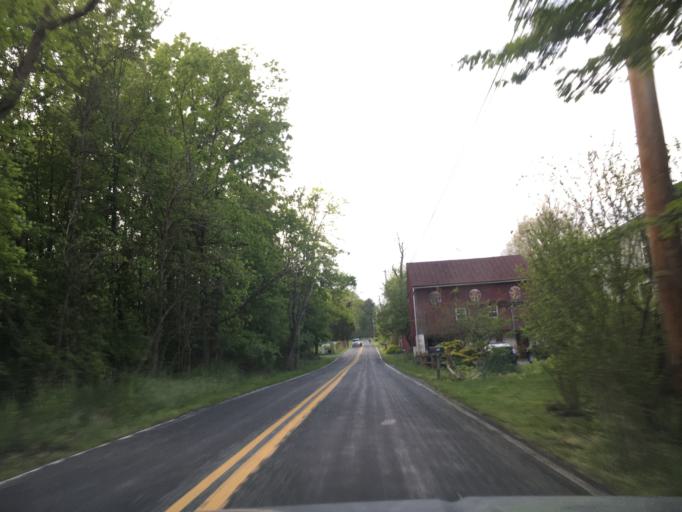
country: US
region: Pennsylvania
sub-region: Berks County
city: Fleetwood
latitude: 40.4494
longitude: -75.7805
